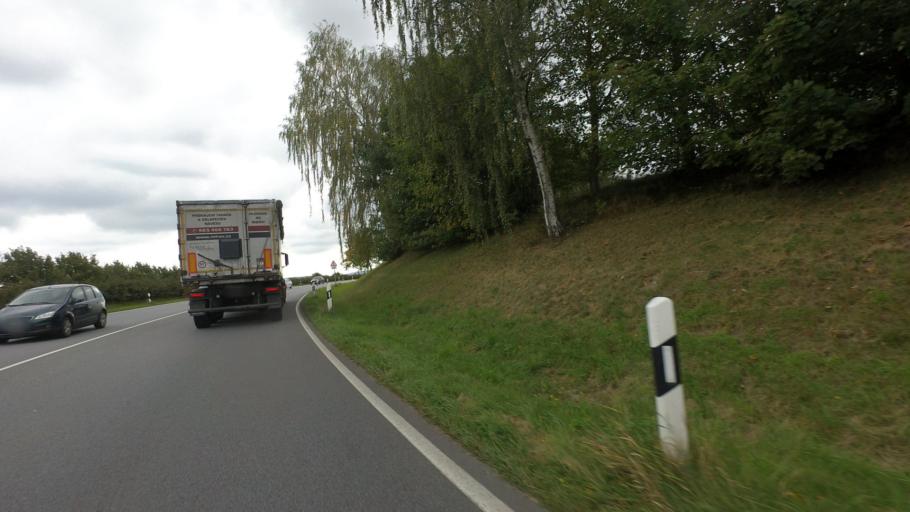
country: DE
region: Saxony
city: Bautzen
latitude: 51.1890
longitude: 14.4151
